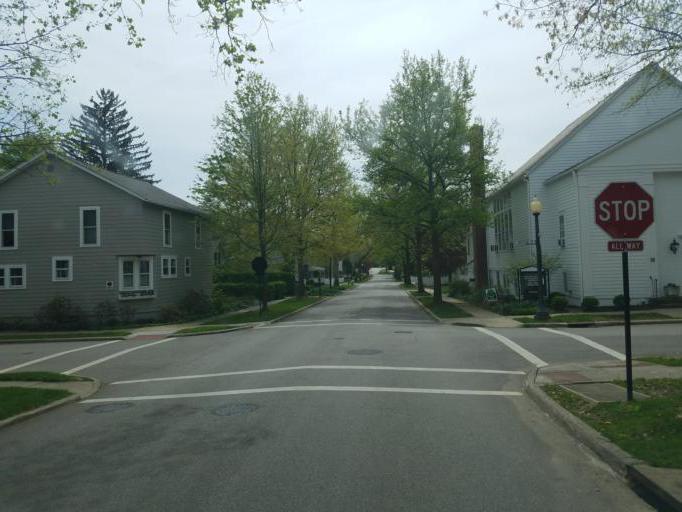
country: US
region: Ohio
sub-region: Summit County
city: Hudson
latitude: 41.2419
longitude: -81.4376
